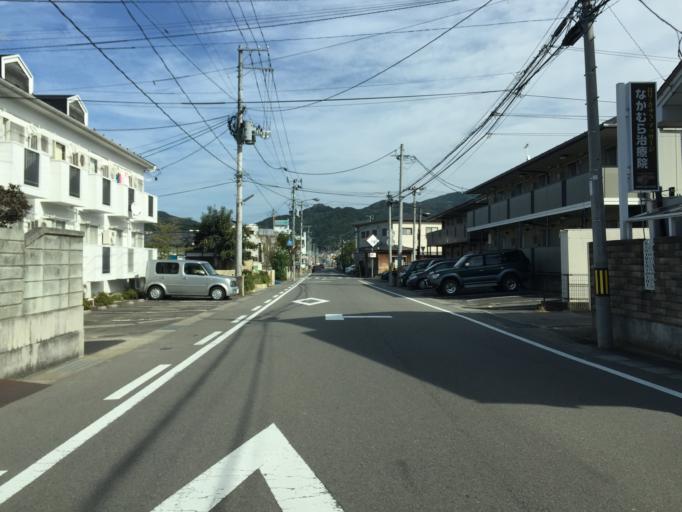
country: JP
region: Fukushima
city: Fukushima-shi
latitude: 37.7476
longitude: 140.4786
